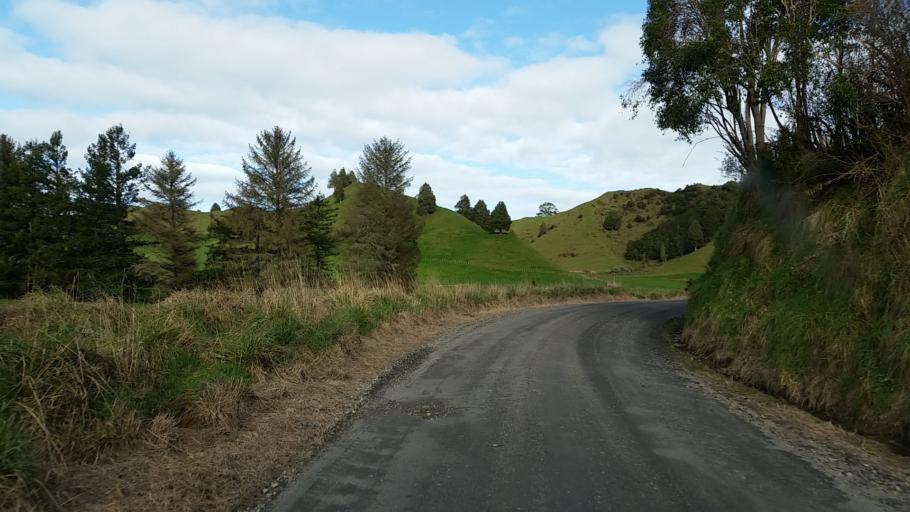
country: NZ
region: Taranaki
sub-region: South Taranaki District
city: Eltham
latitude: -39.2563
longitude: 174.5255
